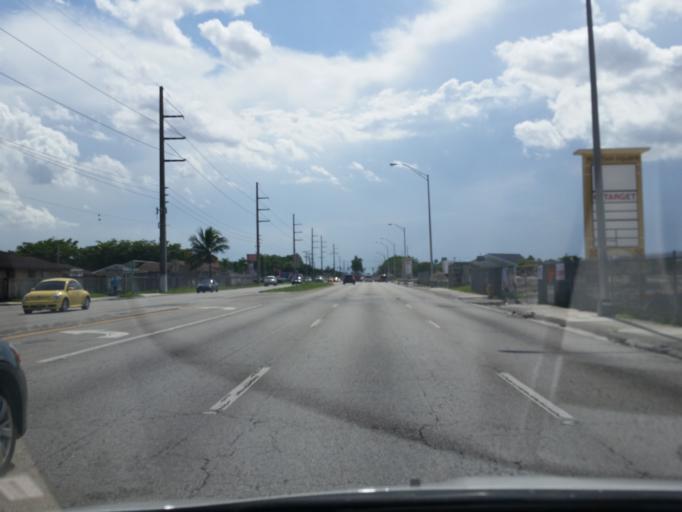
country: US
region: Florida
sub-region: Miami-Dade County
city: Fountainebleau
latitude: 25.7690
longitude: -80.3576
